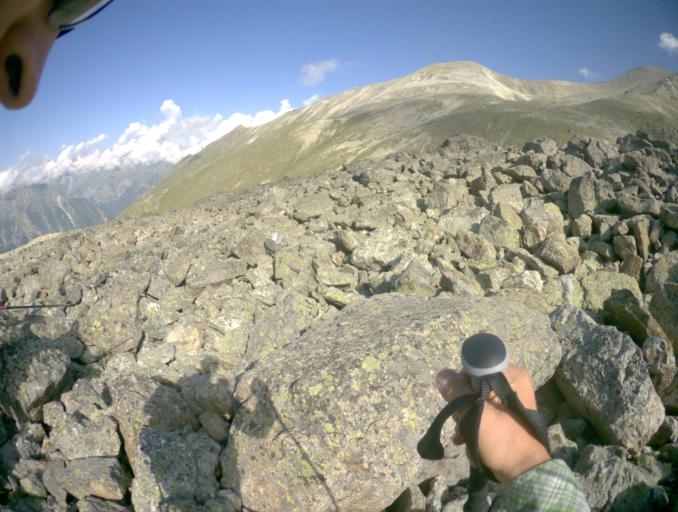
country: RU
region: Karachayevo-Cherkesiya
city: Uchkulan
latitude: 43.3087
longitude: 42.0663
